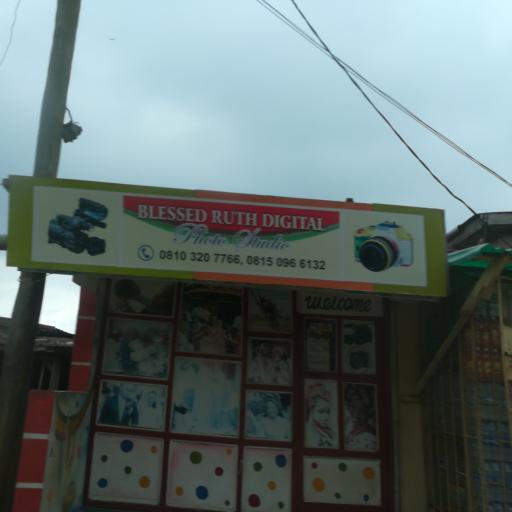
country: NG
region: Lagos
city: Oshodi
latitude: 6.5803
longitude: 3.3040
